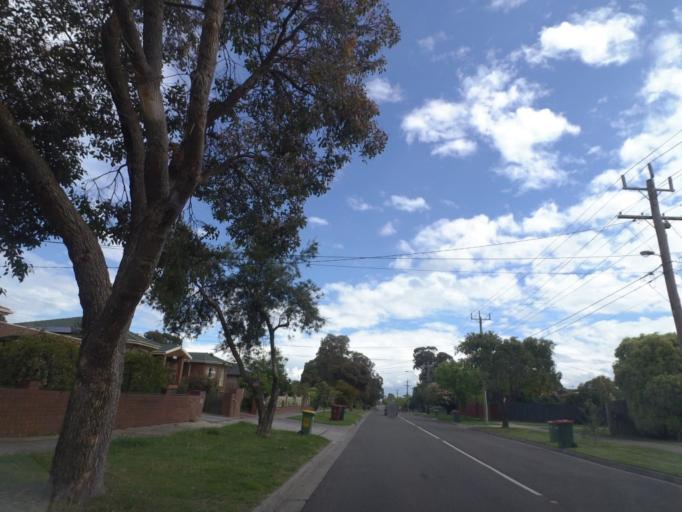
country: AU
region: Victoria
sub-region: Knox
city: Boronia
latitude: -37.8730
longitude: 145.2716
